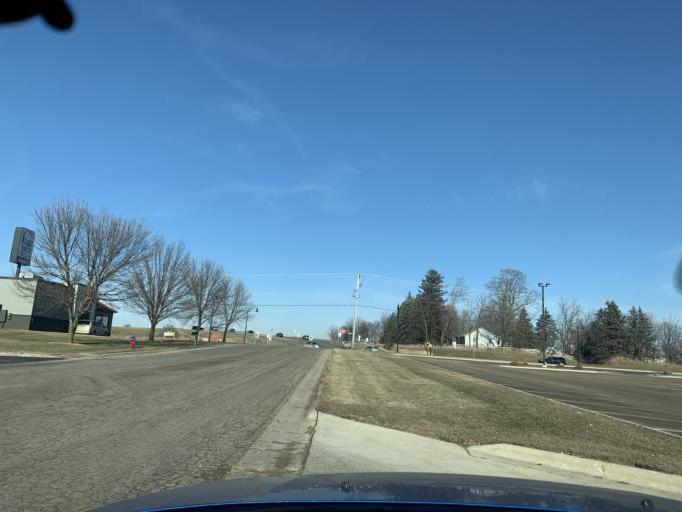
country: US
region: Wisconsin
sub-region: Green County
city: Monroe
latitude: 42.6026
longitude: -89.6642
